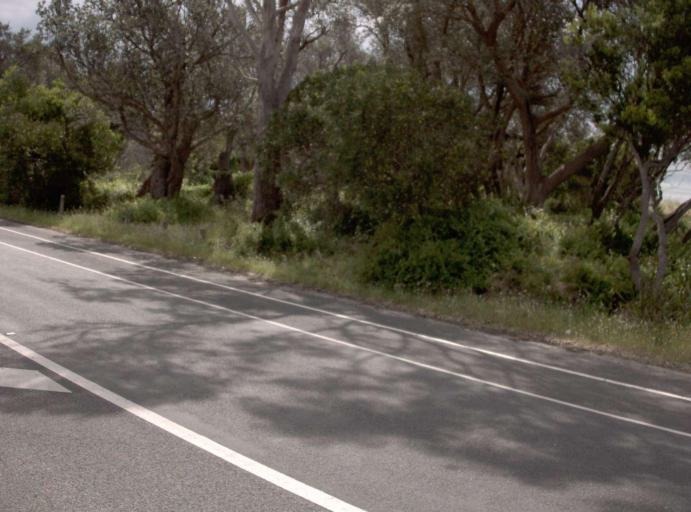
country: AU
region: Victoria
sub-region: Mornington Peninsula
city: Tootgarook
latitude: -38.3709
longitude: 144.8388
